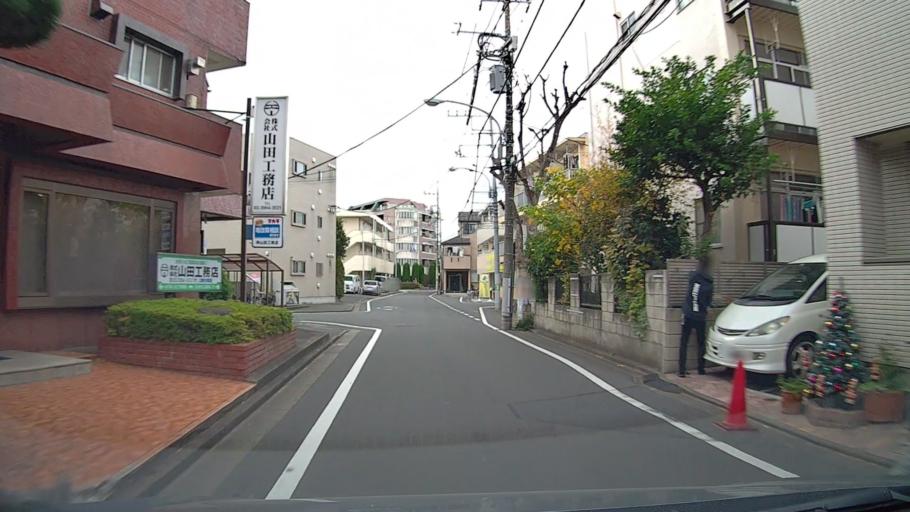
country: JP
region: Saitama
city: Wako
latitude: 35.7327
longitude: 139.6117
